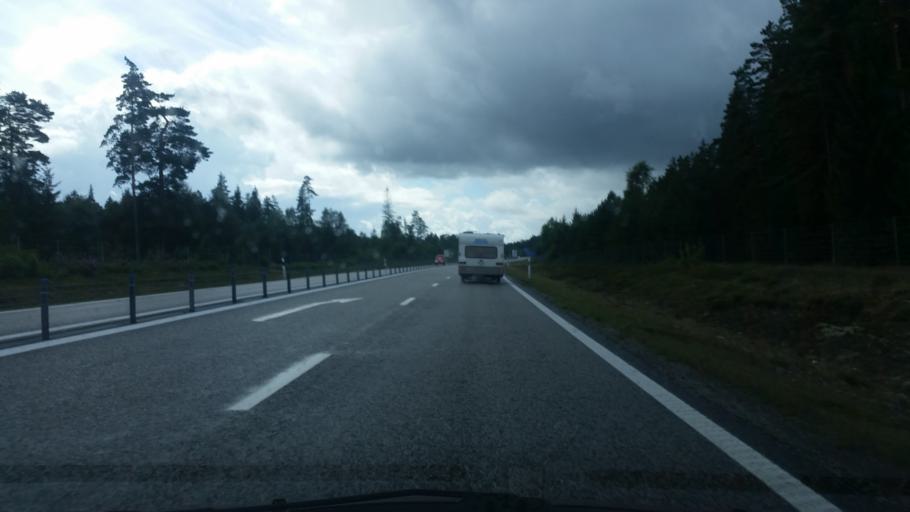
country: SE
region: Joenkoeping
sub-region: Gislaveds Kommun
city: Gislaved
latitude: 57.3475
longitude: 13.5554
